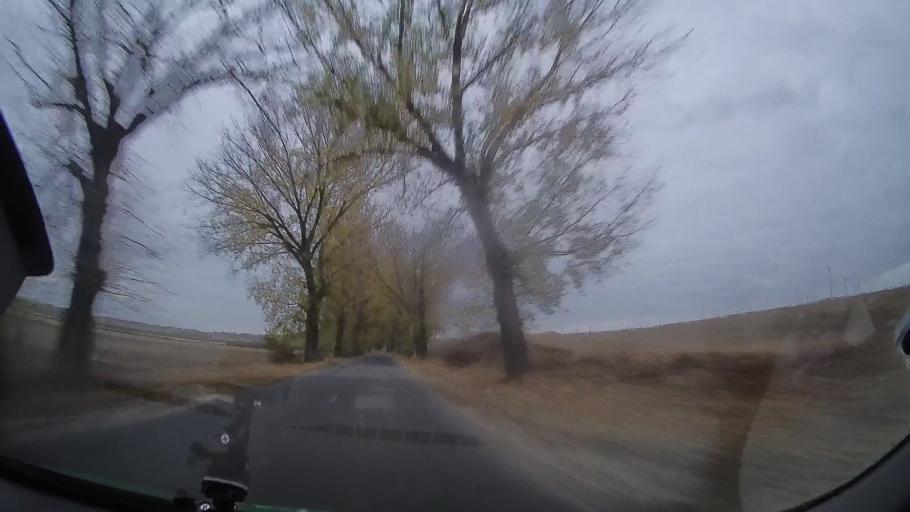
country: RO
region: Tulcea
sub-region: Comuna Mihai Bravu
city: Mihai Bravu
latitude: 44.9633
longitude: 28.6381
